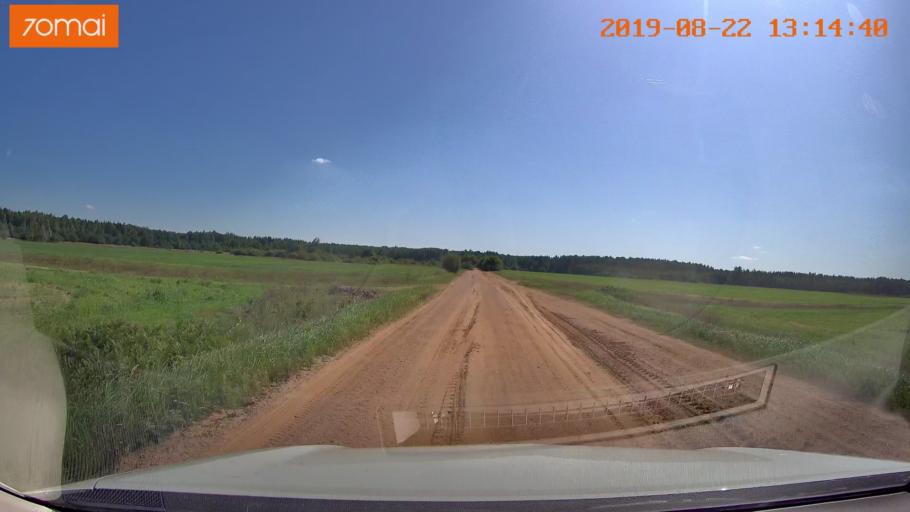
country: BY
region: Minsk
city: Prawdzinski
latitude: 53.2657
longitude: 27.8898
